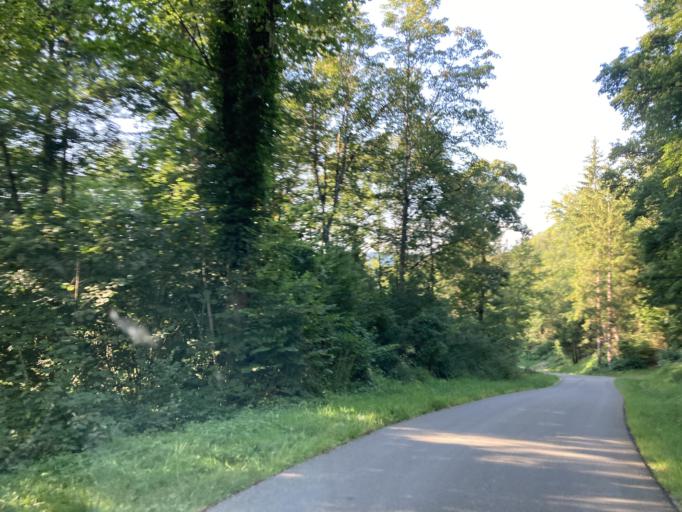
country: DE
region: Baden-Wuerttemberg
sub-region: Freiburg Region
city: Blumberg
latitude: 47.8168
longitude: 8.5135
